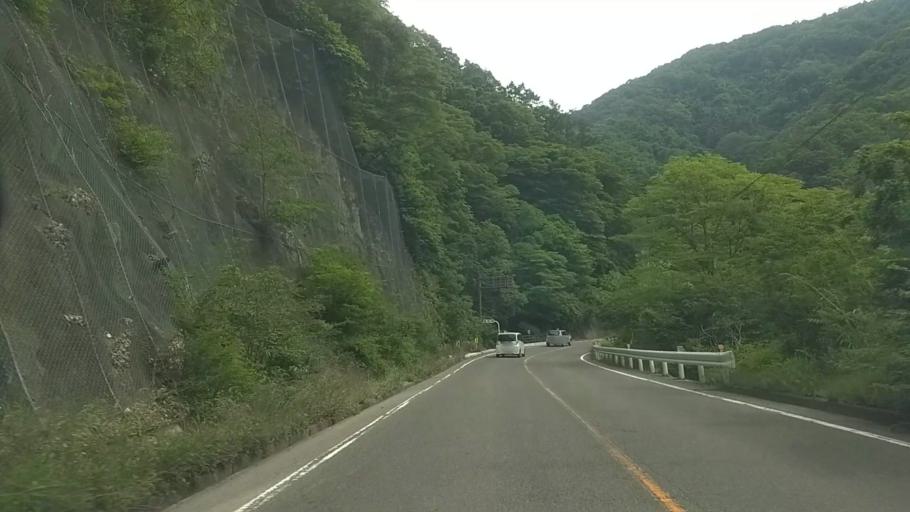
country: JP
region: Yamanashi
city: Isawa
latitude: 35.5595
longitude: 138.5900
